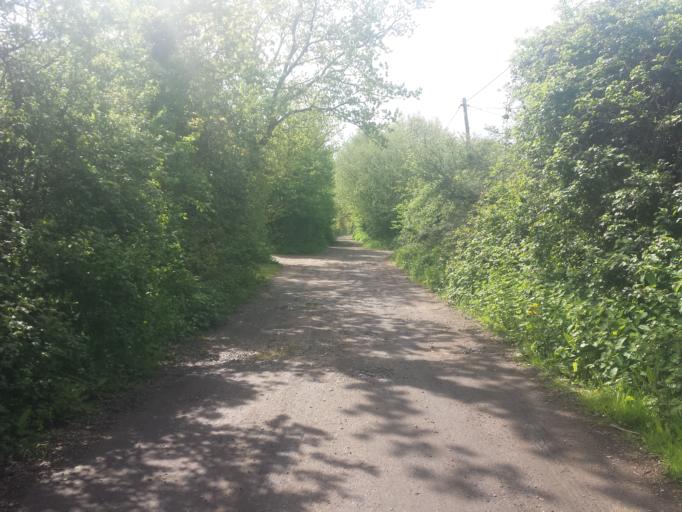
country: GB
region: England
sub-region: Essex
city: Great Bentley
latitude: 51.8823
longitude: 1.0440
